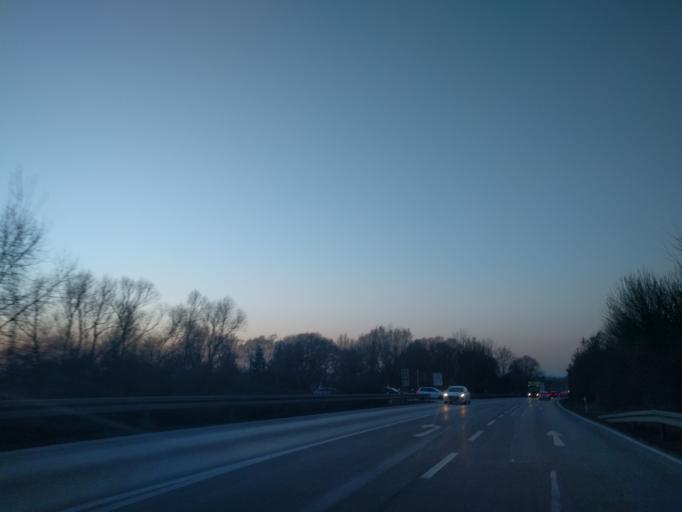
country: DE
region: Bavaria
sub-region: Swabia
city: Donauwoerth
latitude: 48.7052
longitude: 10.7712
